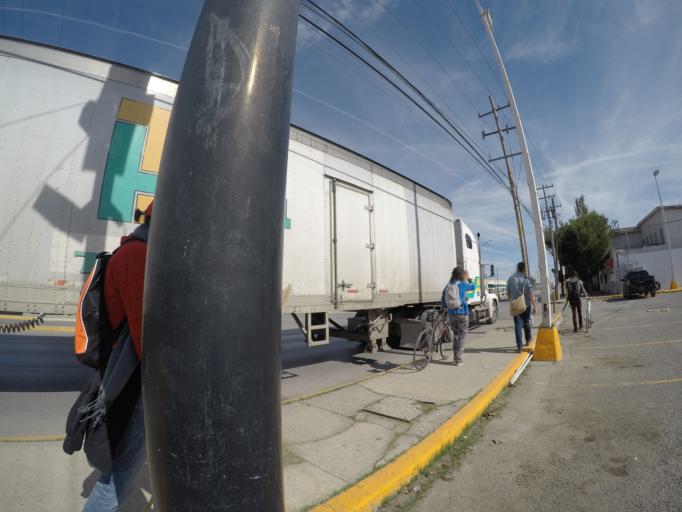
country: MX
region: Chihuahua
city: Ciudad Juarez
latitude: 31.7338
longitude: -106.4481
